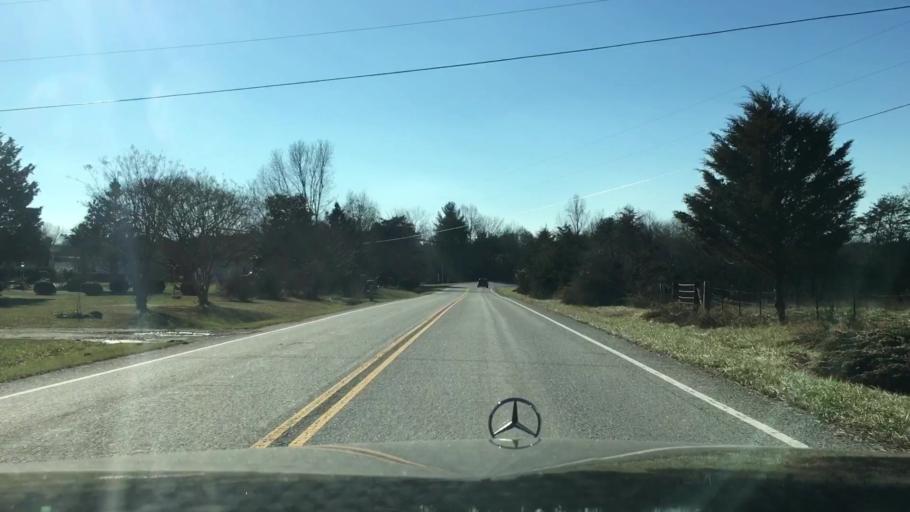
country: US
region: Virginia
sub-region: City of Bedford
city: Bedford
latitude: 37.2274
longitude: -79.5396
